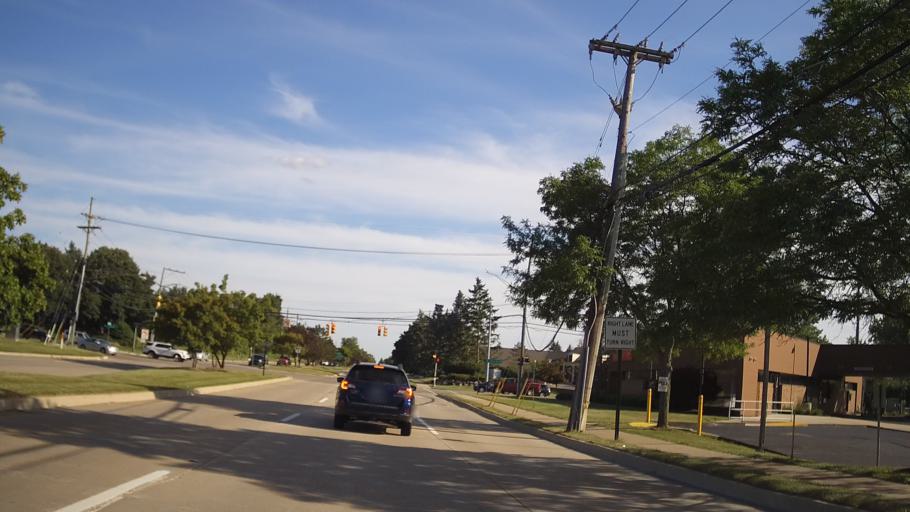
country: US
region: Michigan
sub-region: Oakland County
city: Troy
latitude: 42.5914
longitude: -83.1884
